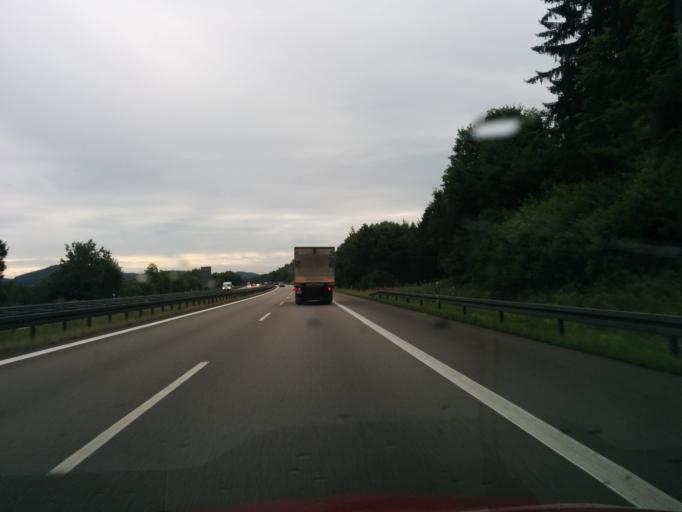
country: DE
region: Bavaria
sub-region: Upper Palatinate
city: Velburg
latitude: 49.2586
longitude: 11.6077
